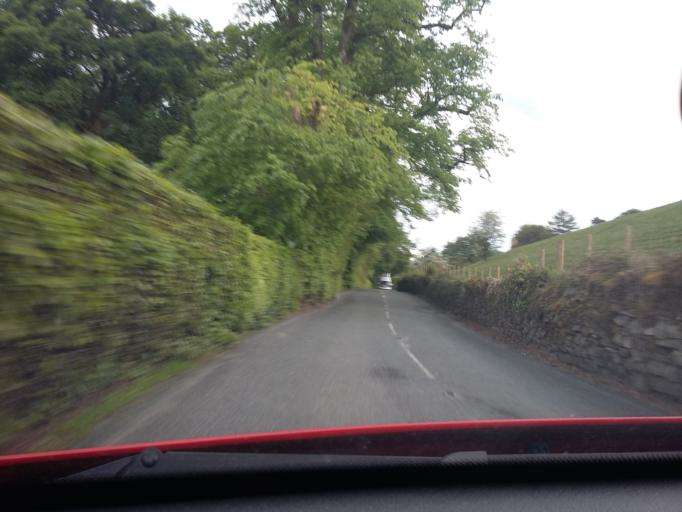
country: GB
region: England
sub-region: Cumbria
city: Windermere
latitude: 54.3882
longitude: -2.9143
